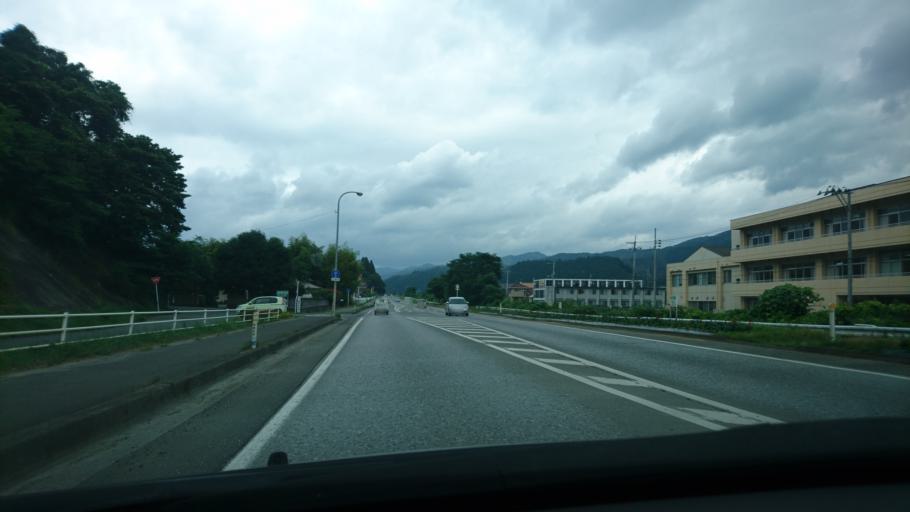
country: JP
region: Iwate
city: Ofunato
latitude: 38.9052
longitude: 141.5487
